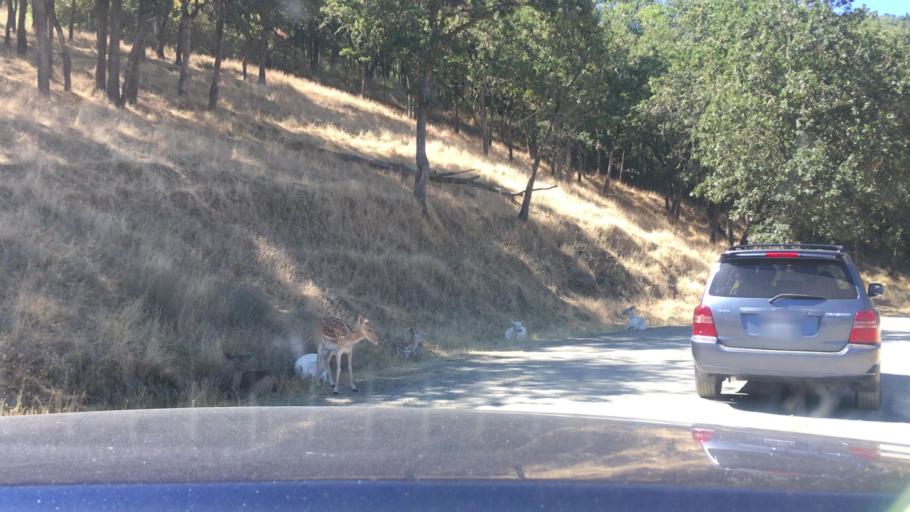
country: US
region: Oregon
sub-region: Douglas County
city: Winston
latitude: 43.1390
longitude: -123.4343
